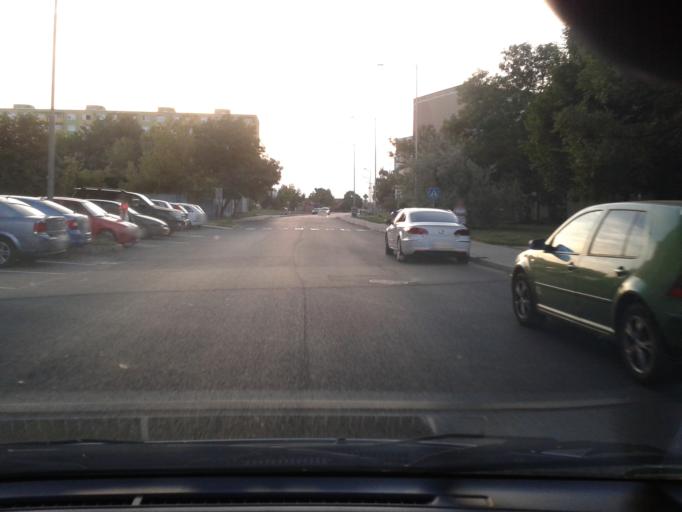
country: SK
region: Nitriansky
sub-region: Okres Nove Zamky
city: Sturovo
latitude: 47.7920
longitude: 18.7209
